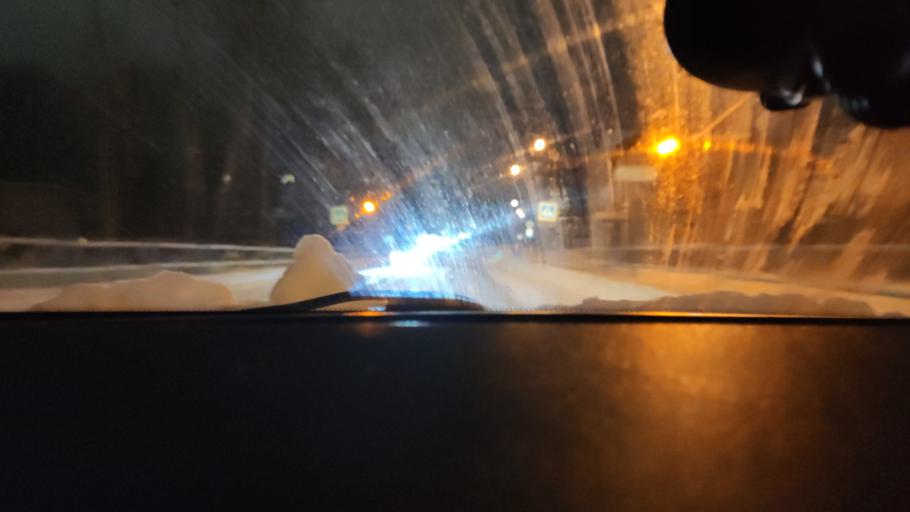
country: RU
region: Perm
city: Krasnokamsk
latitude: 58.0847
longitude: 55.7664
